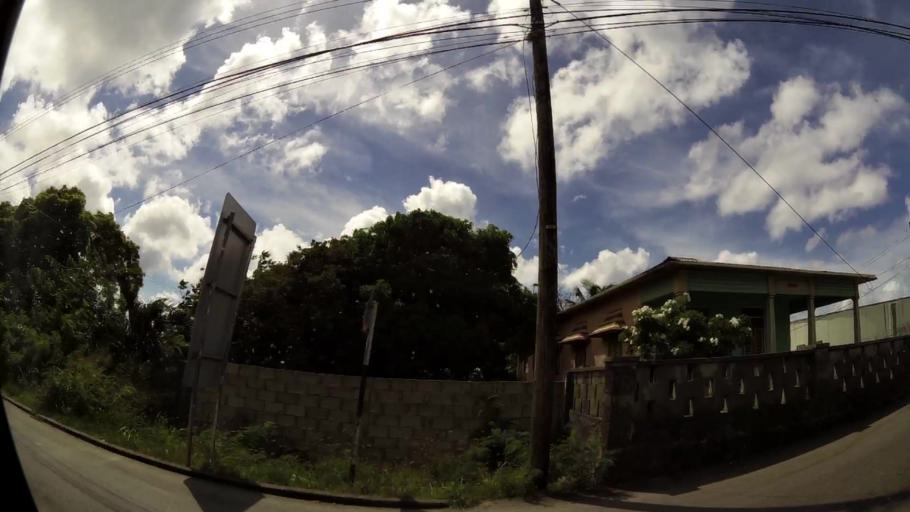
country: BB
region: Saint Michael
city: Bridgetown
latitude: 13.1349
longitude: -59.6229
